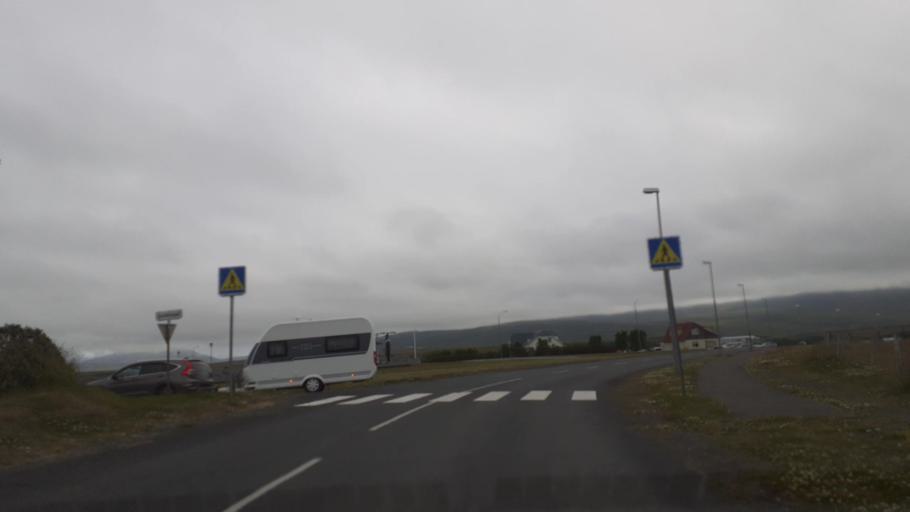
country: IS
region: Northwest
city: Saudarkrokur
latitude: 65.6570
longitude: -20.3005
